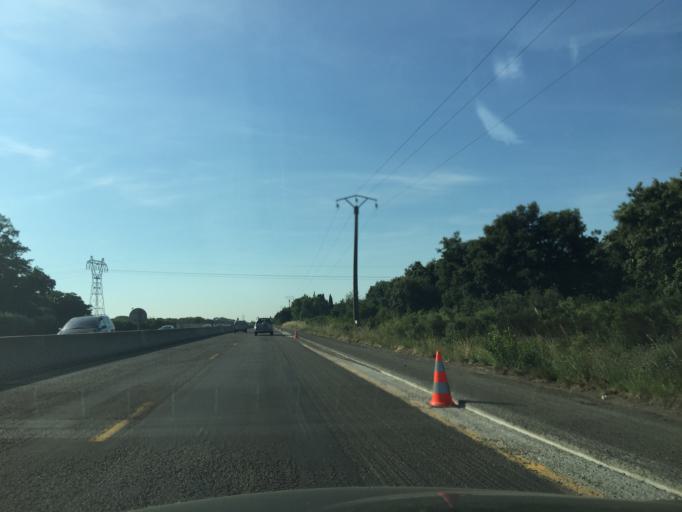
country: FR
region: Provence-Alpes-Cote d'Azur
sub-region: Departement des Bouches-du-Rhone
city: Fos-sur-Mer
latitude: 43.4636
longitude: 4.9173
